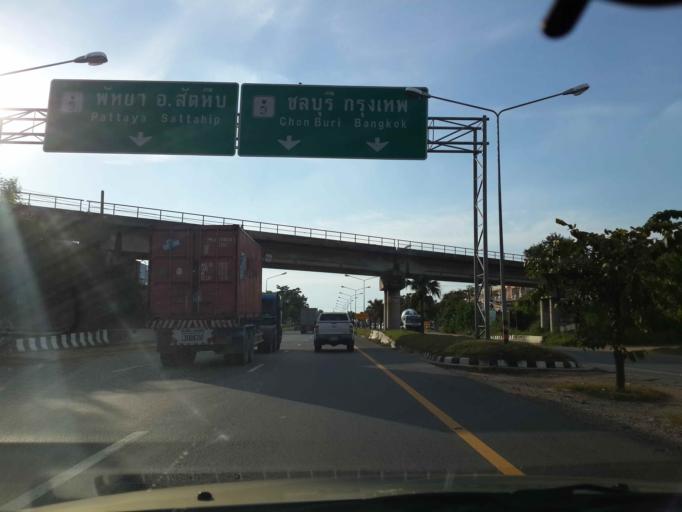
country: TH
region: Chon Buri
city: Bang Lamung
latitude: 12.9978
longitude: 100.9343
